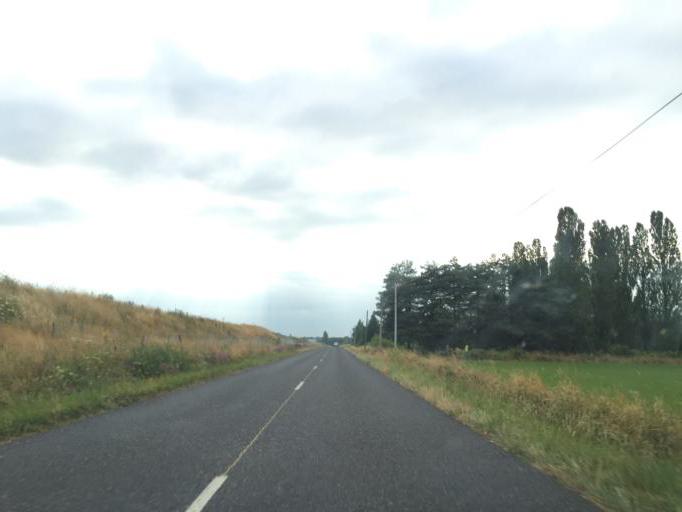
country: FR
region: Auvergne
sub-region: Departement de l'Allier
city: Neuilly-le-Real
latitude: 46.5375
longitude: 3.4334
